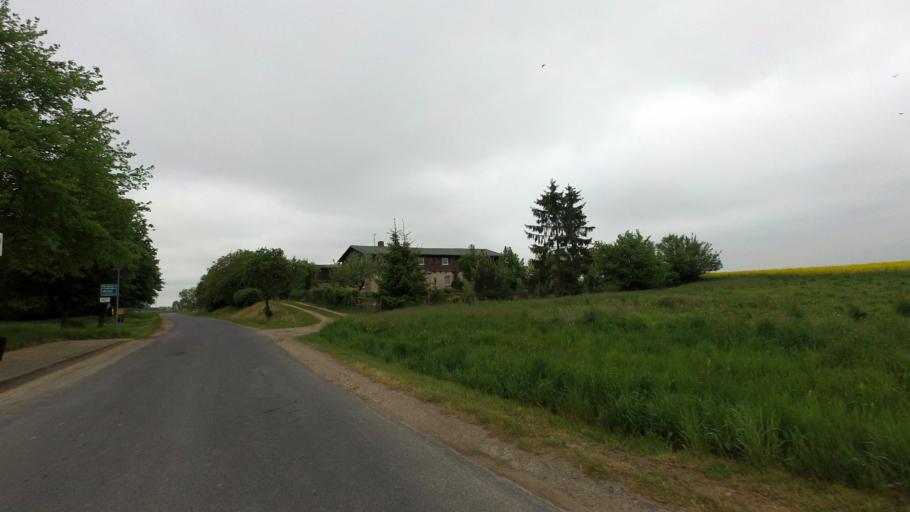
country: DE
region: Mecklenburg-Vorpommern
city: Mollenhagen
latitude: 53.6032
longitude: 12.9294
